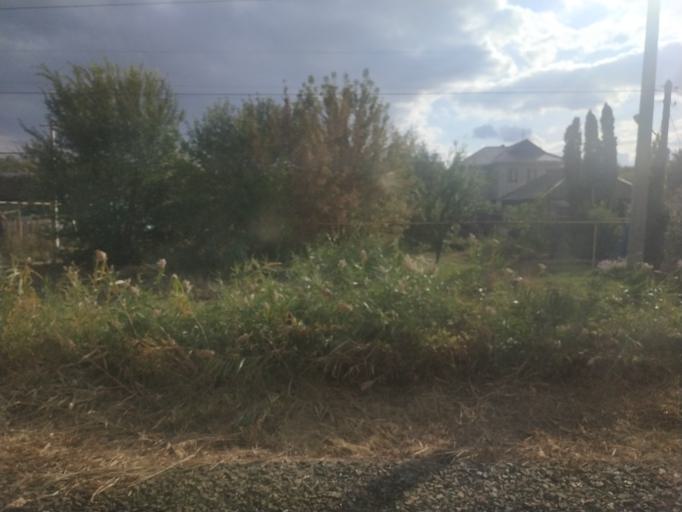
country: RU
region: Volgograd
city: Krasnoslobodsk
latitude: 48.5094
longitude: 44.5337
